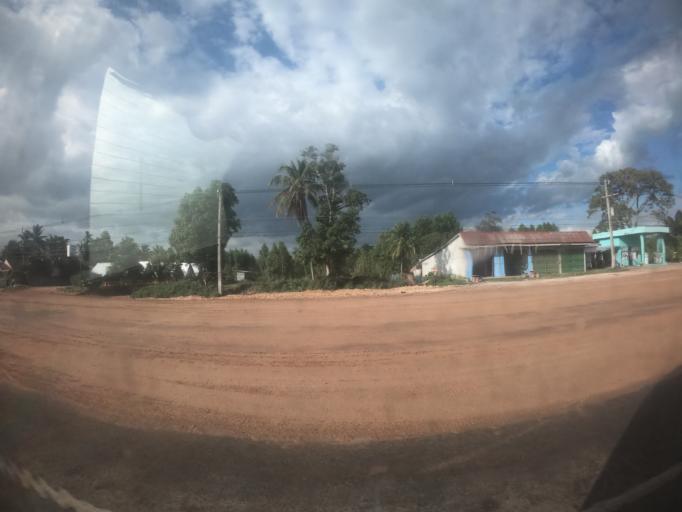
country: TH
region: Surin
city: Kap Choeng
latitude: 14.4804
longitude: 103.5851
